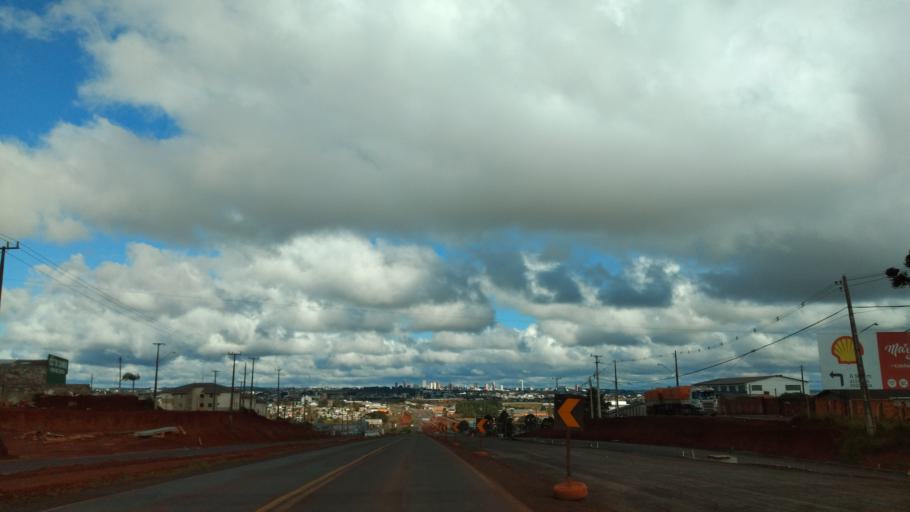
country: BR
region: Parana
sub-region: Guarapuava
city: Guarapuava
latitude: -25.3450
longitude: -51.4902
